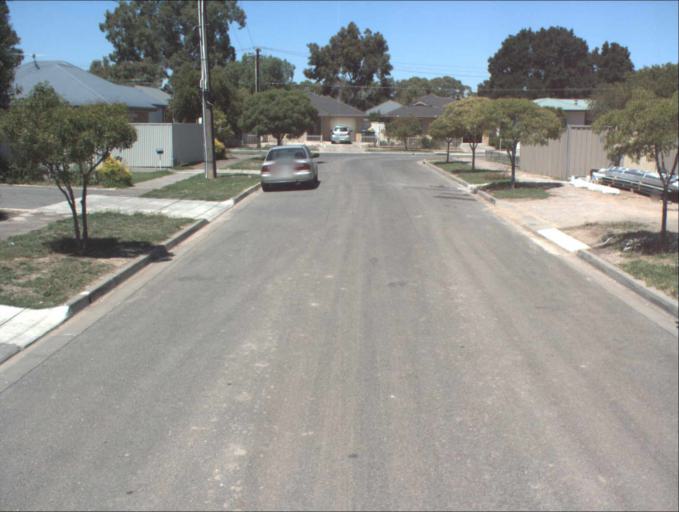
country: AU
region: South Australia
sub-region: Port Adelaide Enfield
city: Klemzig
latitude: -34.8677
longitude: 138.6266
